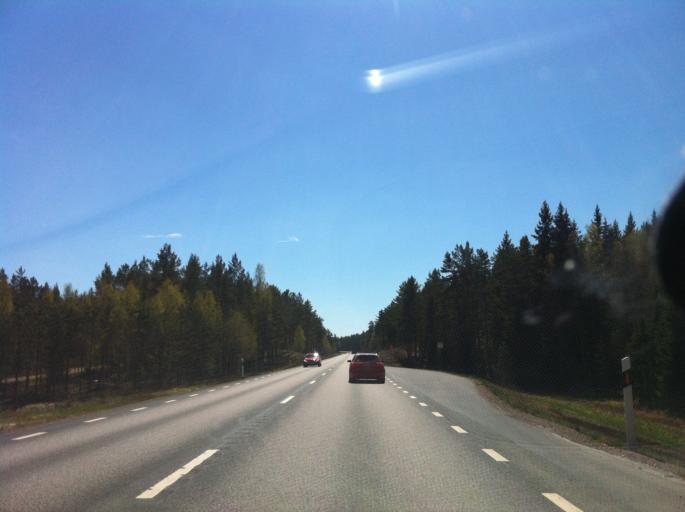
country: SE
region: Kalmar
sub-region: Vimmerby Kommun
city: Vimmerby
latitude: 57.6473
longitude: 15.8377
